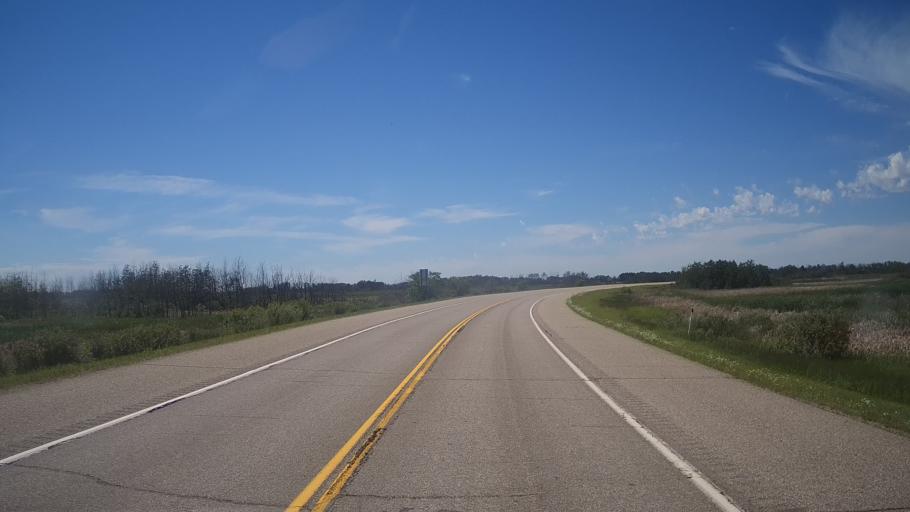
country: CA
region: Saskatchewan
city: Langenburg
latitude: 50.7715
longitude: -101.4940
